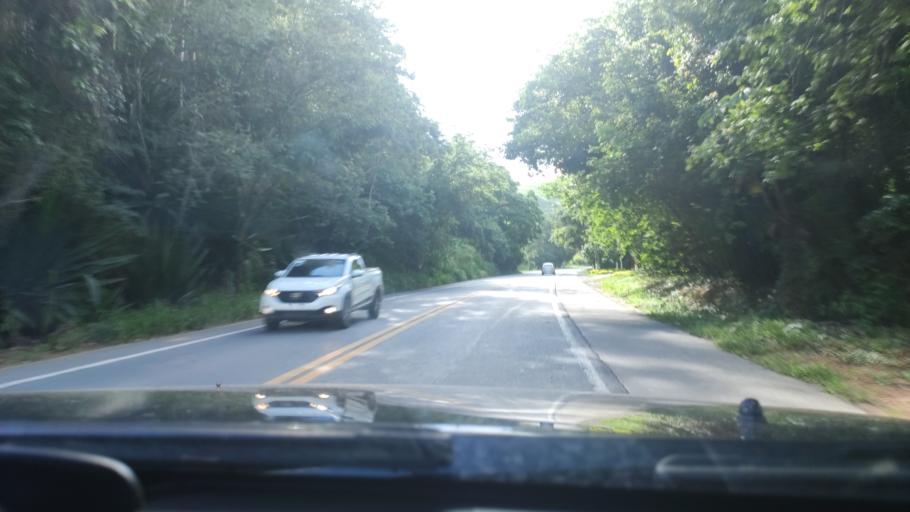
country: BR
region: Sao Paulo
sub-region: Aguas De Lindoia
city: Aguas de Lindoia
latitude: -22.5193
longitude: -46.6631
